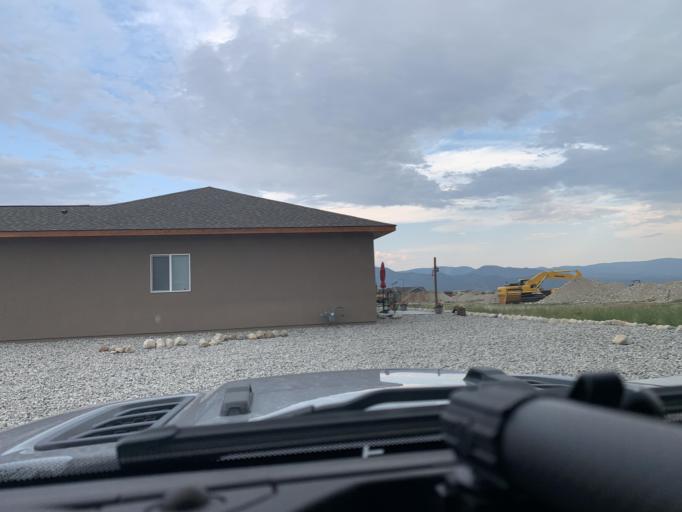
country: US
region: Colorado
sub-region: Chaffee County
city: Buena Vista
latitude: 38.8310
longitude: -106.1552
